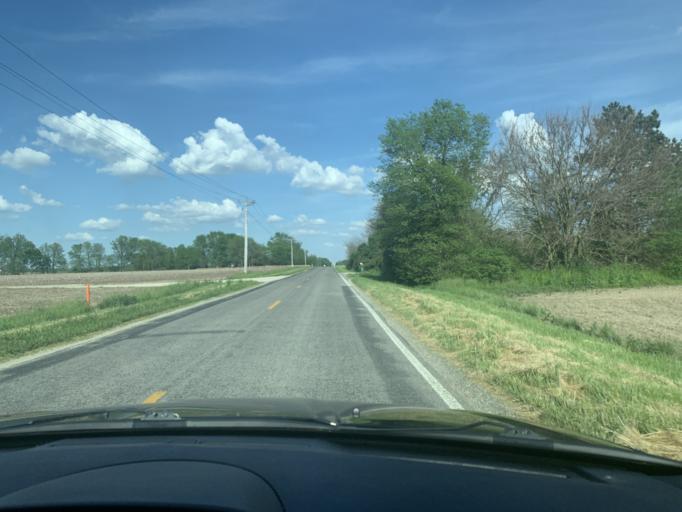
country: US
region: Ohio
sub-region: Logan County
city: De Graff
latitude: 40.2424
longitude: -83.9852
